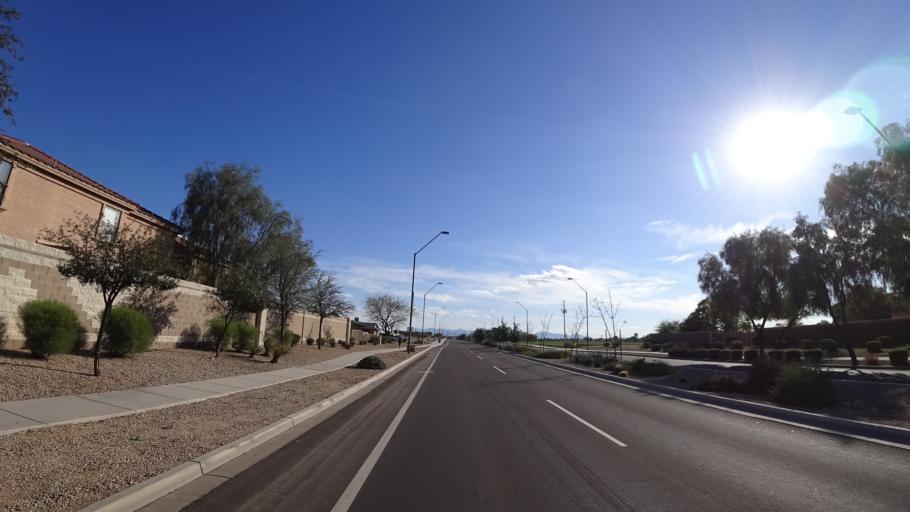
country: US
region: Arizona
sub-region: Maricopa County
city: Peoria
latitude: 33.5707
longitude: -112.2376
